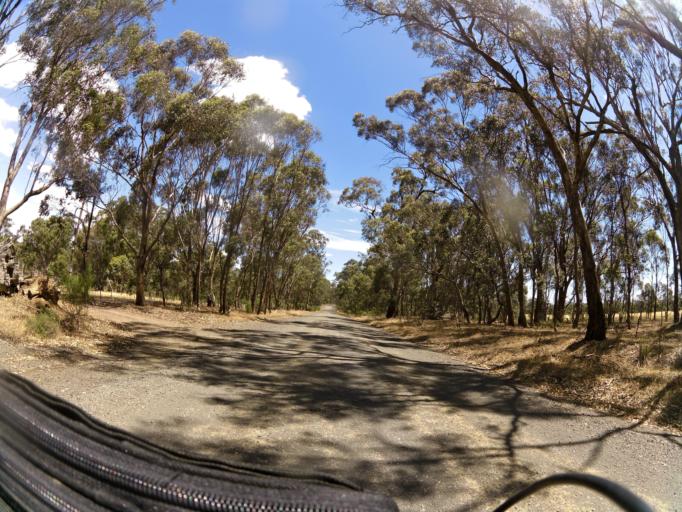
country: AU
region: Victoria
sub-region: Campaspe
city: Kyabram
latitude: -36.7985
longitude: 145.0792
